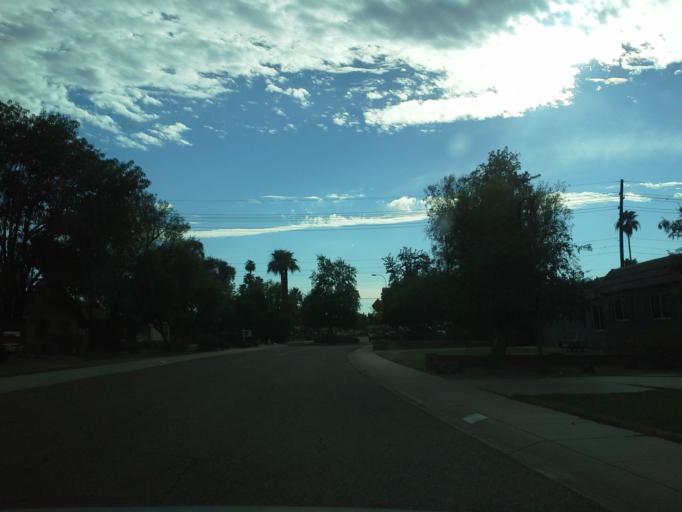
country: US
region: Arizona
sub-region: Maricopa County
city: Glendale
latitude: 33.5659
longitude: -112.0903
